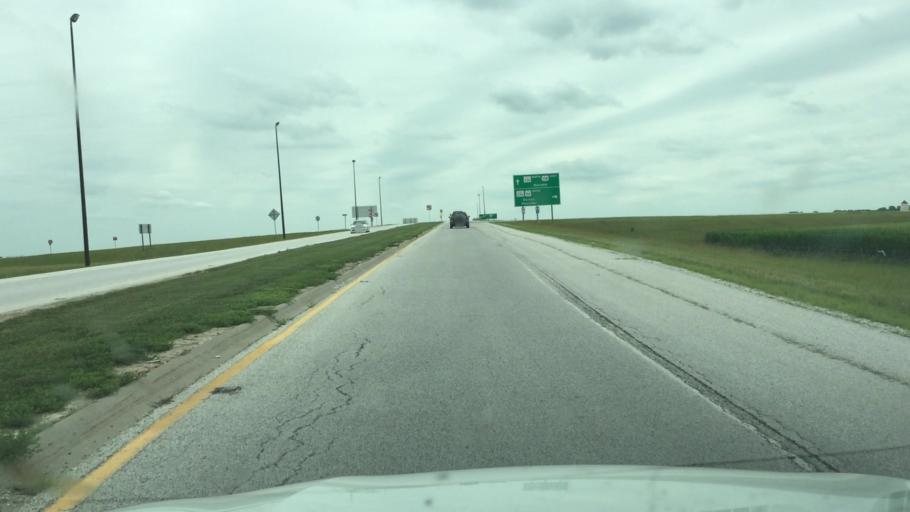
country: US
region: Illinois
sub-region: Hancock County
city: Carthage
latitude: 40.4150
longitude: -91.1150
